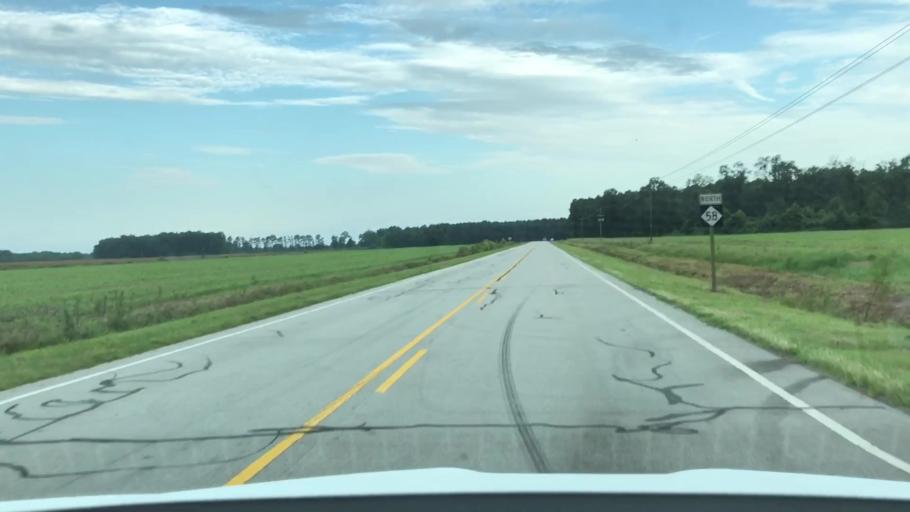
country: US
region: North Carolina
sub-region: Jones County
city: Trenton
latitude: 35.1067
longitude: -77.5004
